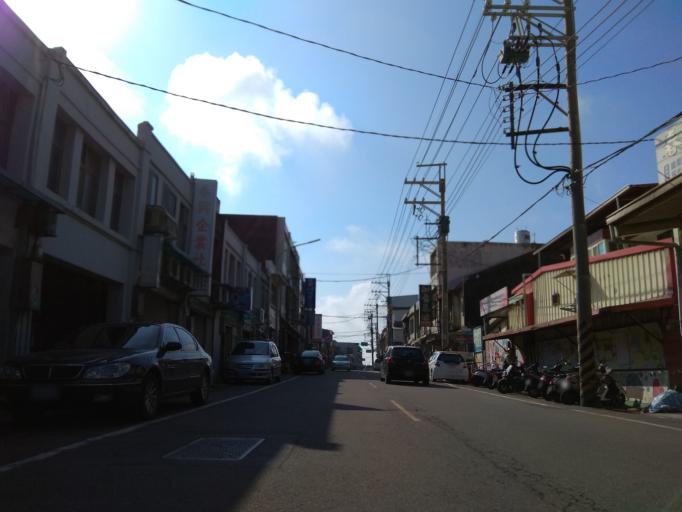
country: TW
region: Taiwan
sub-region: Hsinchu
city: Zhubei
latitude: 25.0368
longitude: 121.0801
